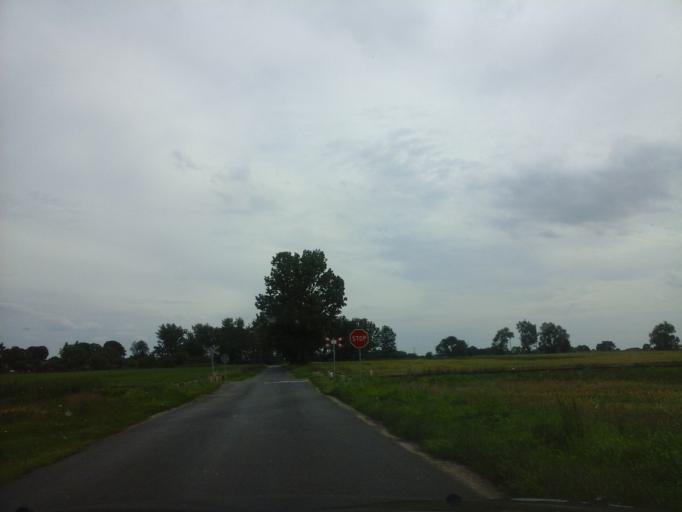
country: PL
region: West Pomeranian Voivodeship
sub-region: Powiat stargardzki
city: Stara Dabrowa
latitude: 53.3532
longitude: 15.1317
